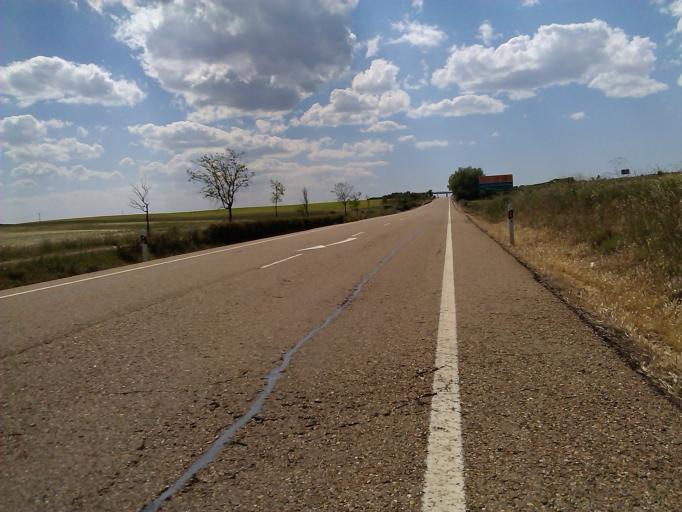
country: ES
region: Castille and Leon
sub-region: Provincia de Palencia
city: Moratinos
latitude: 42.3655
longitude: -4.9638
